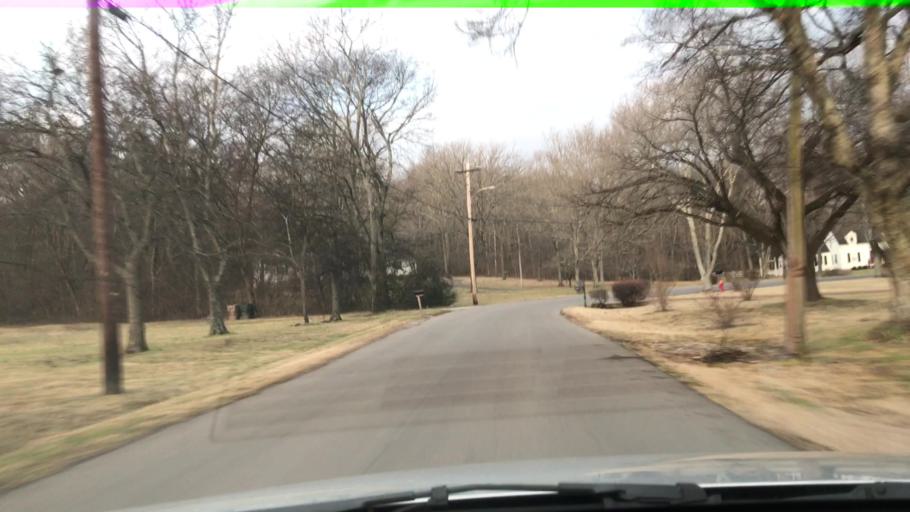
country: US
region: Tennessee
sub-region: Williamson County
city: Brentwood
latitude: 36.0354
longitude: -86.7708
